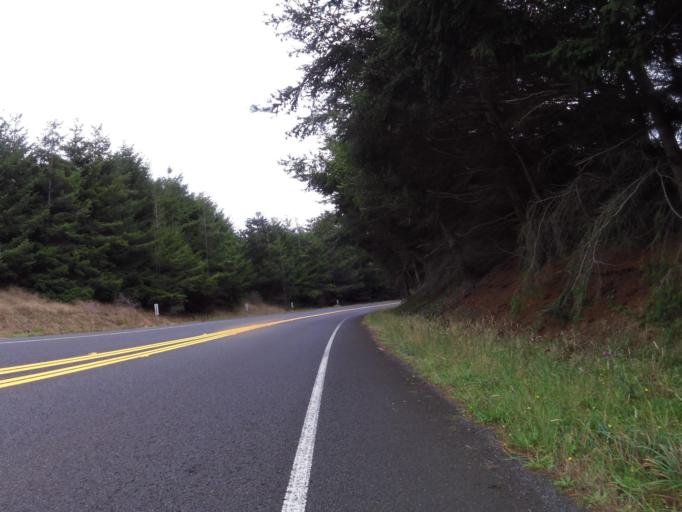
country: US
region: California
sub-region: Sonoma County
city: Monte Rio
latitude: 38.5181
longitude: -123.2446
